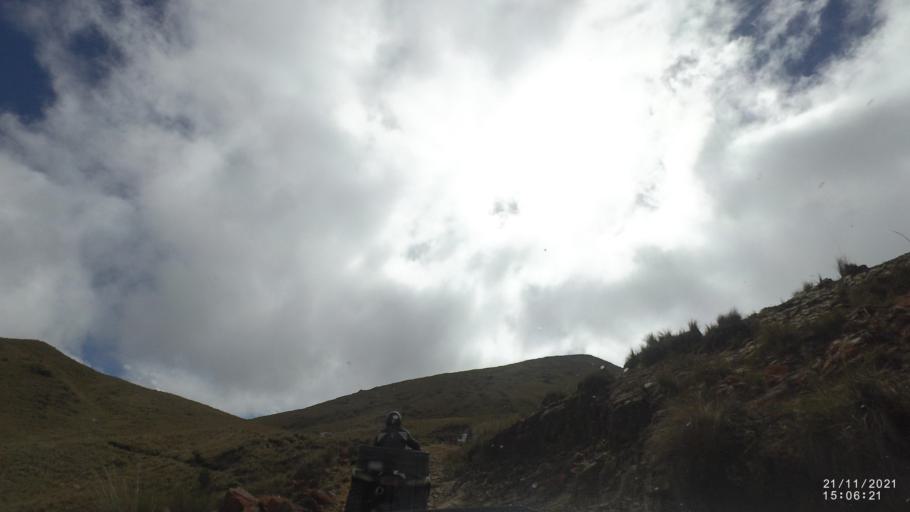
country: BO
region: Cochabamba
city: Cochabamba
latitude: -16.9510
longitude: -66.2590
